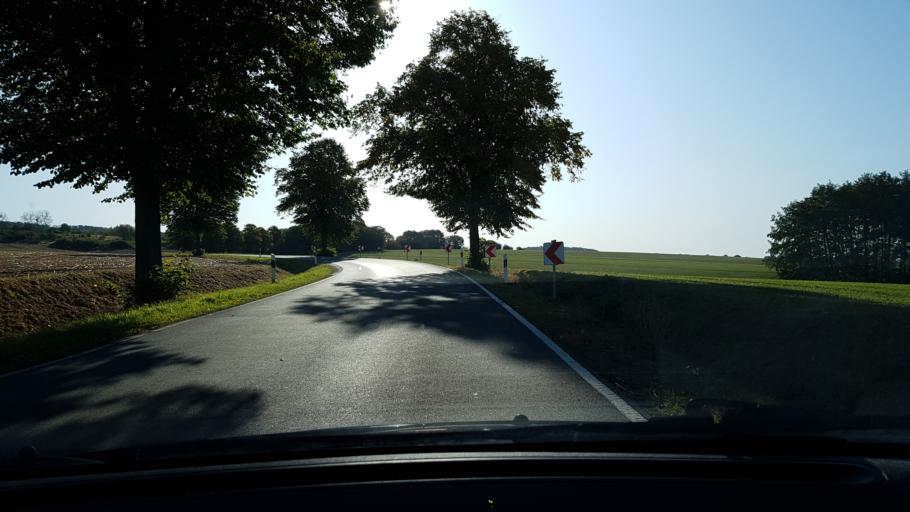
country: DE
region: Lower Saxony
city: Messenkamp
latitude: 52.2581
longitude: 9.3911
